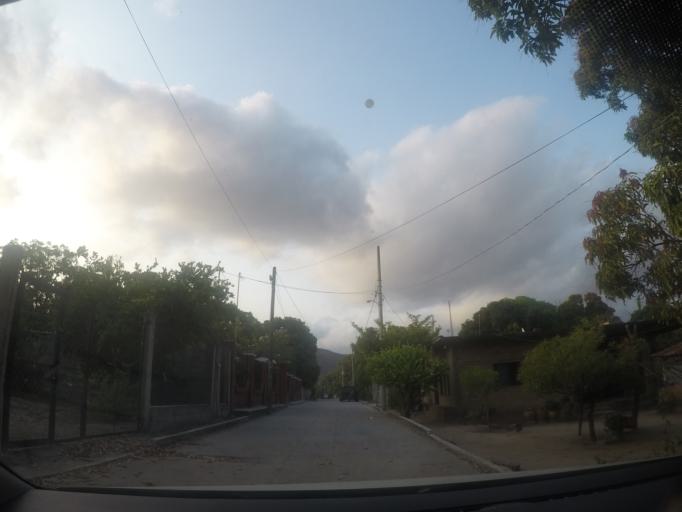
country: MX
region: Oaxaca
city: San Pedro Comitancillo
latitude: 16.5833
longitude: -95.2092
